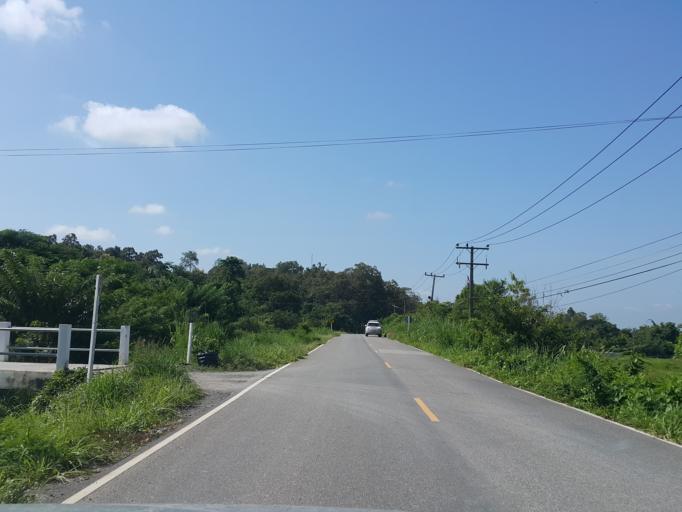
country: TH
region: Chiang Mai
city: San Kamphaeng
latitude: 18.7740
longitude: 99.1742
